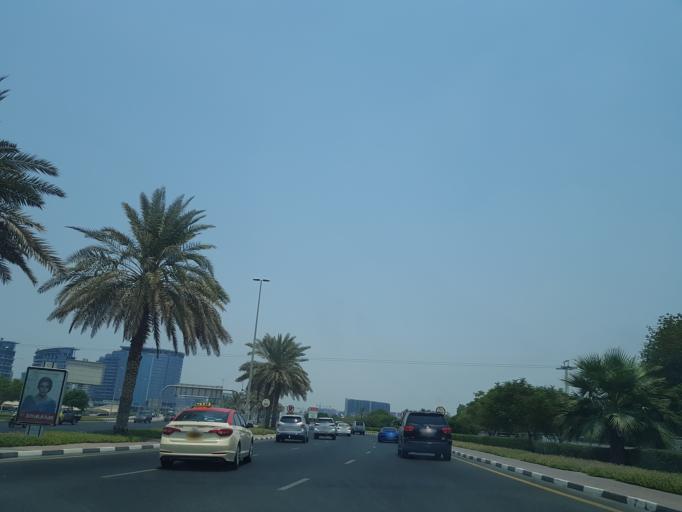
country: AE
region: Ash Shariqah
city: Sharjah
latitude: 25.2459
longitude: 55.3225
